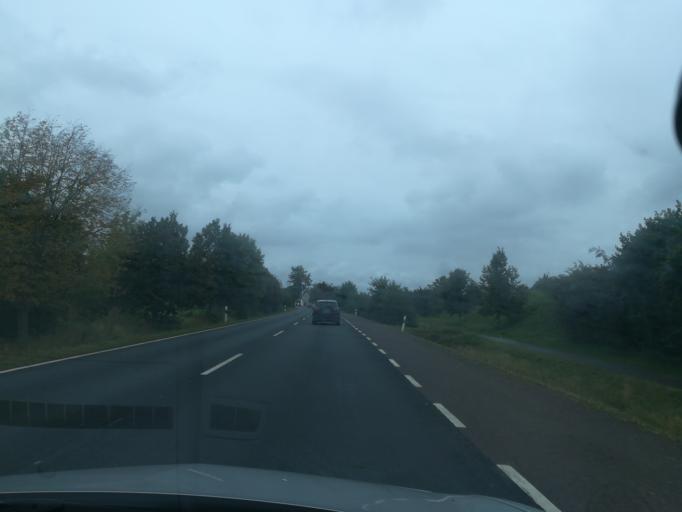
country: DE
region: Saxony-Anhalt
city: Ebendorf
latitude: 52.1884
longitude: 11.5679
